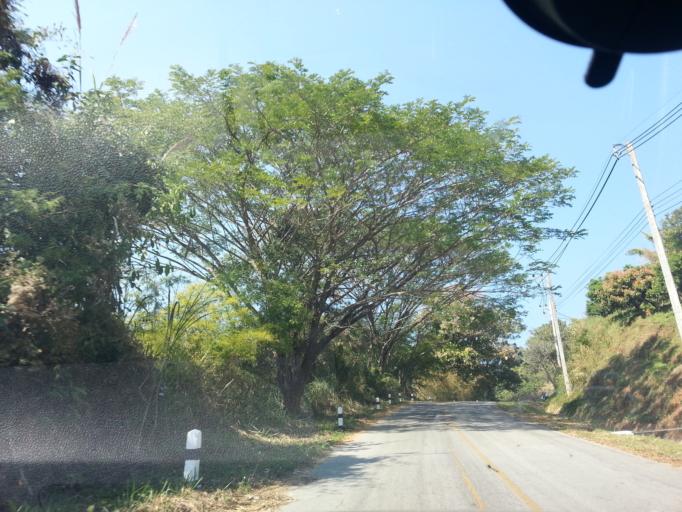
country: TH
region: Chiang Mai
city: Chai Prakan
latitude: 19.8244
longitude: 99.0989
